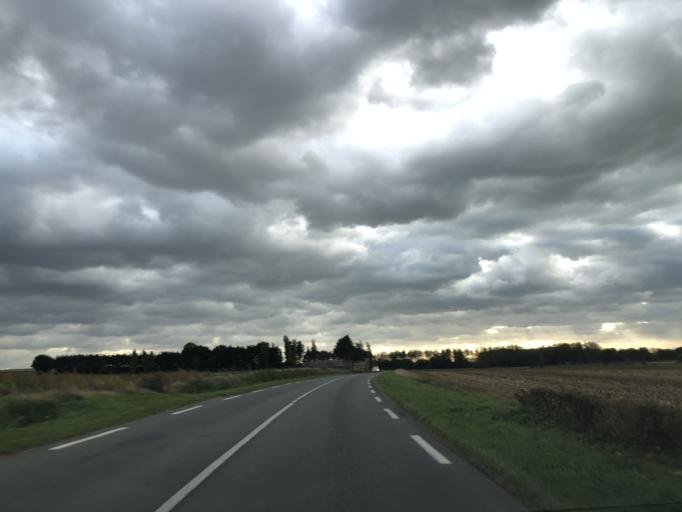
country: FR
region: Picardie
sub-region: Departement de la Somme
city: Cayeux-sur-Mer
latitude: 50.1320
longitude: 1.5059
